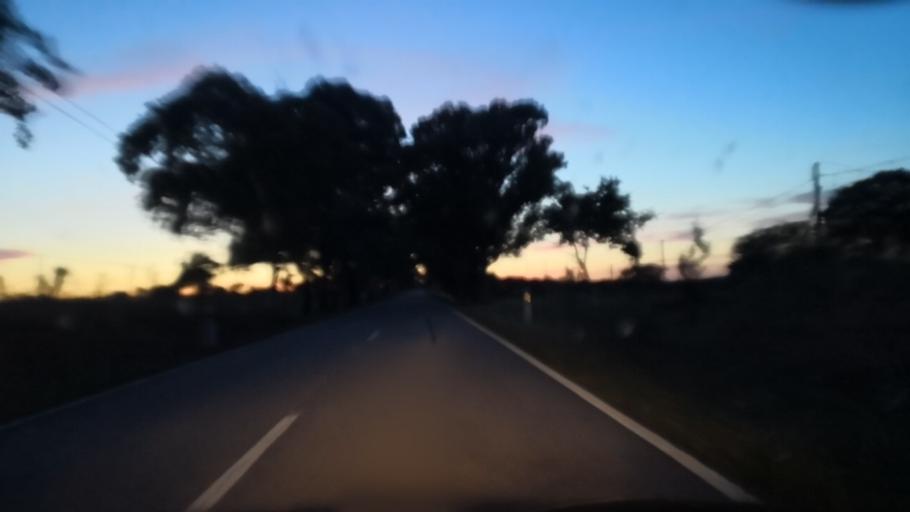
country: ES
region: Extremadura
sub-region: Provincia de Caceres
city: Piedras Albas
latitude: 39.8573
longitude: -6.9975
